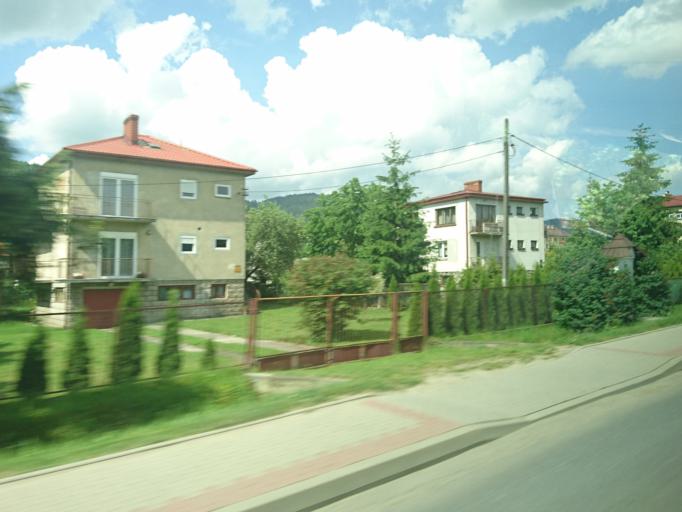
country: PL
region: Lesser Poland Voivodeship
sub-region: Powiat limanowski
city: Kamienica
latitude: 49.5721
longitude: 20.3493
